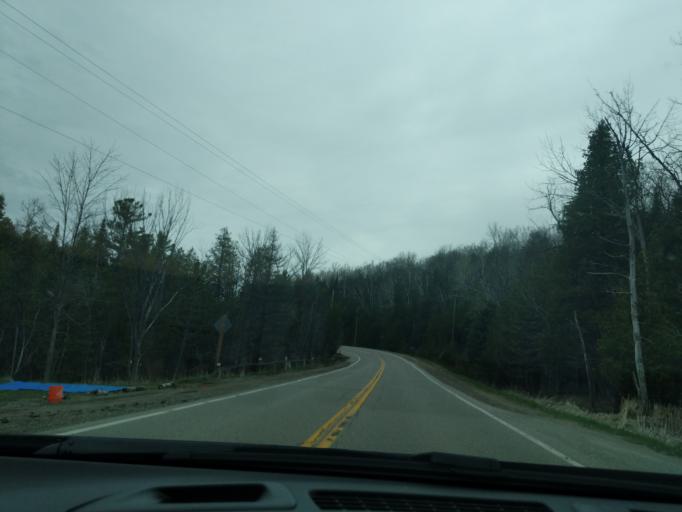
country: CA
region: Ontario
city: Orangeville
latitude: 43.9994
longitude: -80.0010
